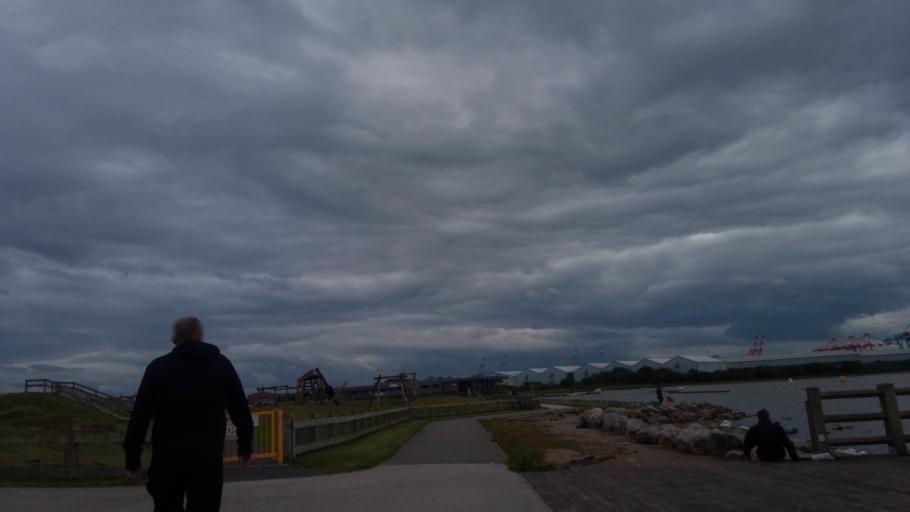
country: GB
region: England
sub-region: Sefton
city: Waterloo
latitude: 53.4722
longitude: -3.0320
